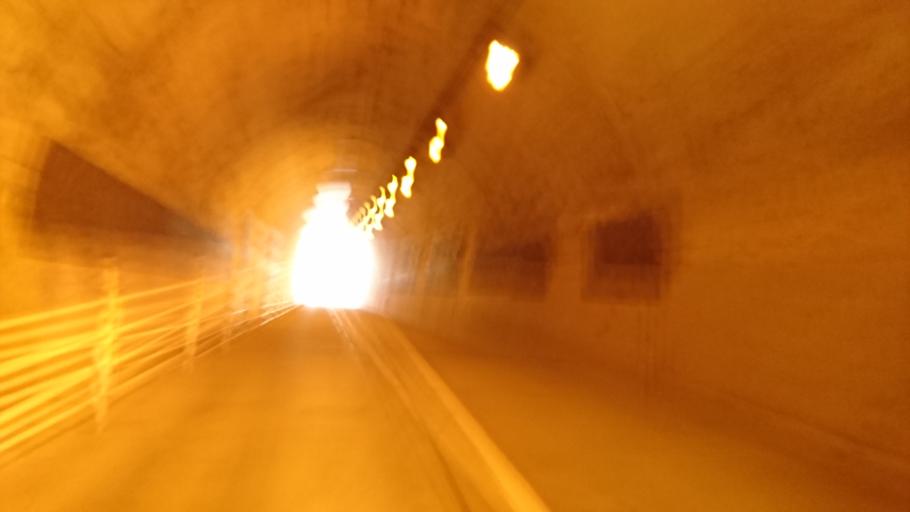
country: JP
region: Hyogo
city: Shirahamacho-usazakiminami
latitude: 34.7930
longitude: 134.7590
